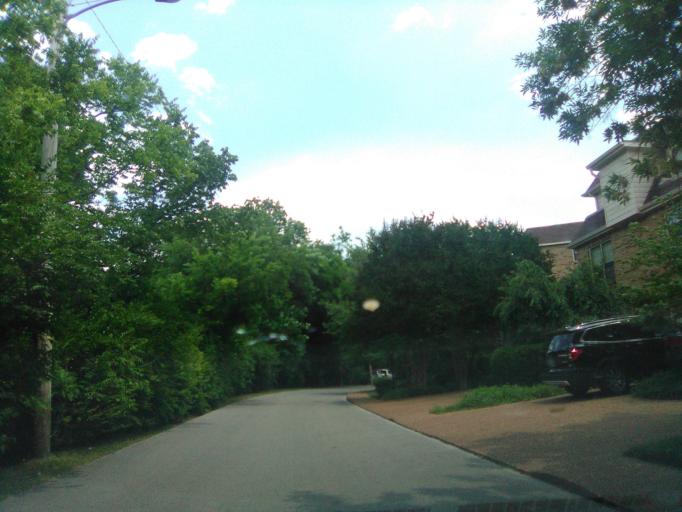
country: US
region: Tennessee
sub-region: Davidson County
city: Belle Meade
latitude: 36.1286
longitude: -86.8280
